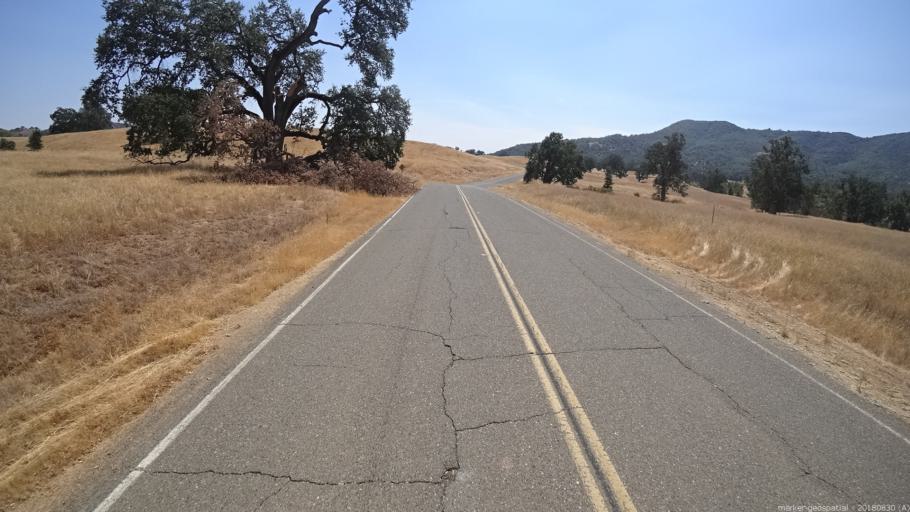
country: US
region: California
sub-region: Monterey County
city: King City
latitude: 35.9759
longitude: -121.3351
